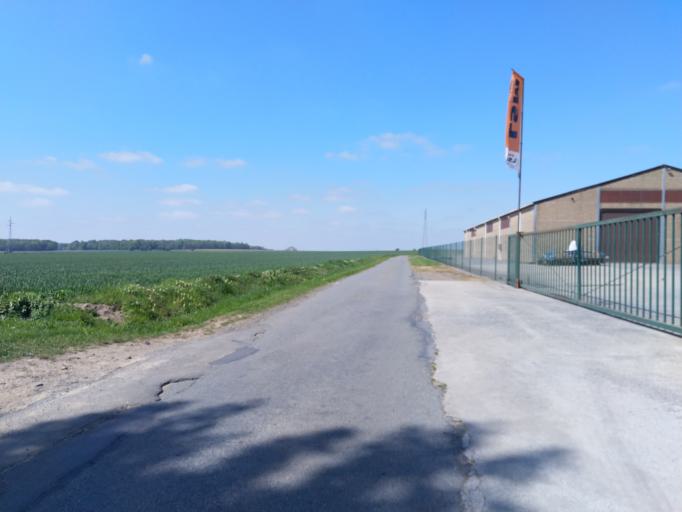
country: BE
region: Wallonia
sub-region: Province du Hainaut
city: Chievres
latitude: 50.5198
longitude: 3.8236
